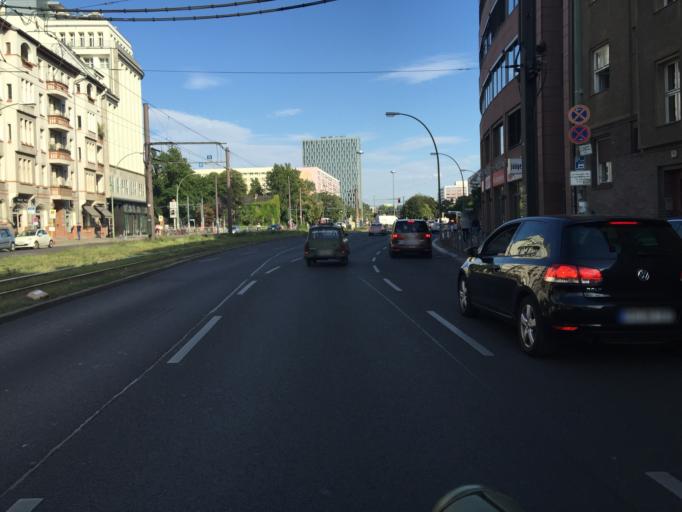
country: DE
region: Berlin
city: Berlin
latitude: 52.5276
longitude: 13.4139
